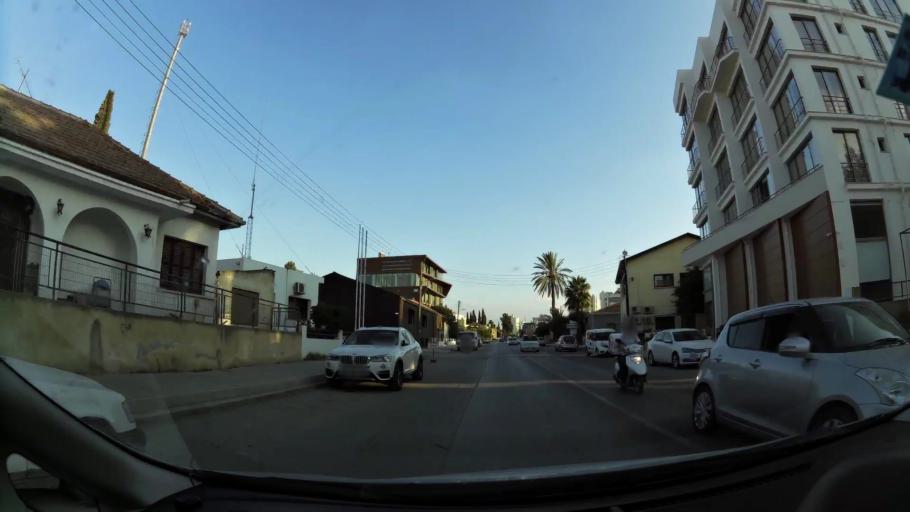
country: CY
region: Lefkosia
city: Nicosia
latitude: 35.1927
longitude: 33.3566
